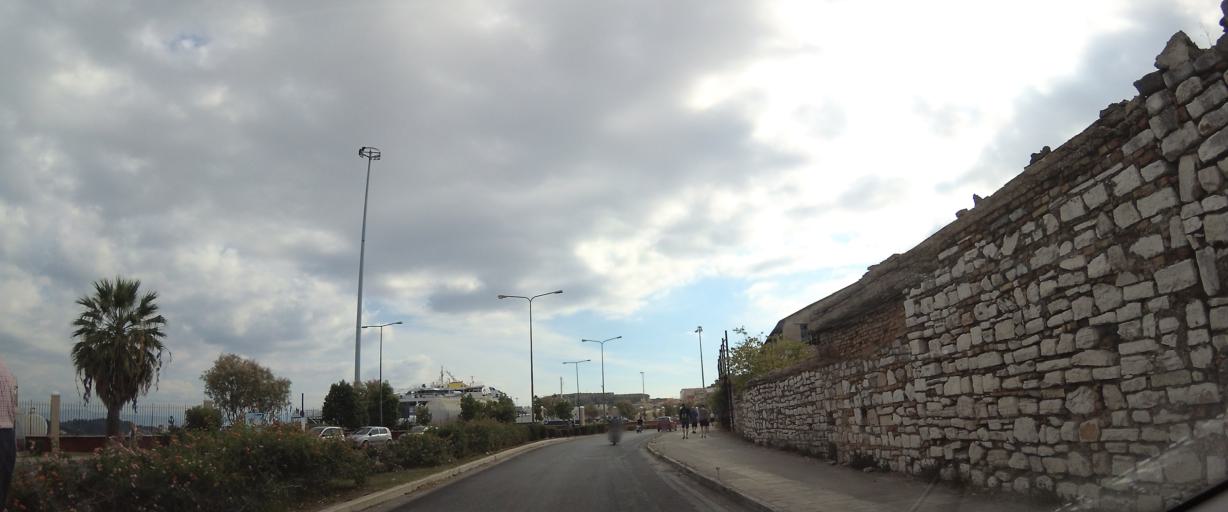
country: GR
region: Ionian Islands
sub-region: Nomos Kerkyras
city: Alepou
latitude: 39.6266
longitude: 19.9058
